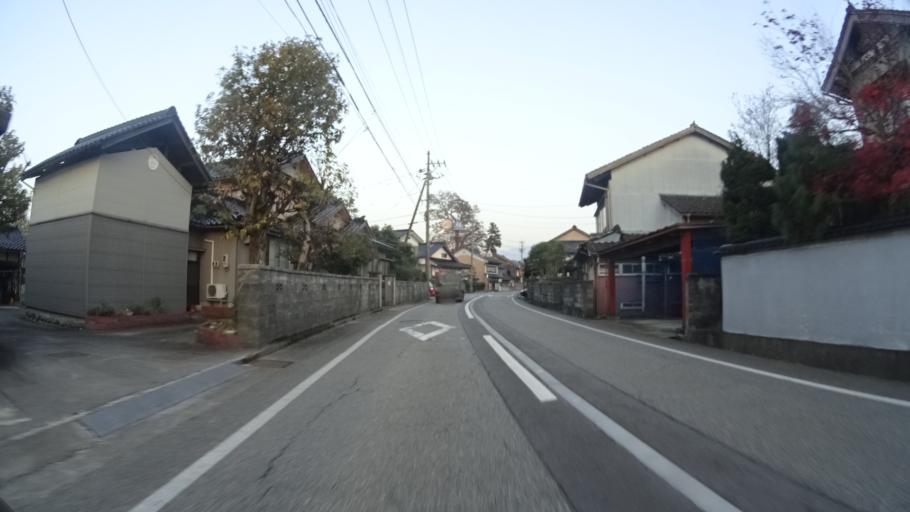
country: JP
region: Toyama
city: Kamiichi
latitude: 36.7068
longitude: 137.3556
